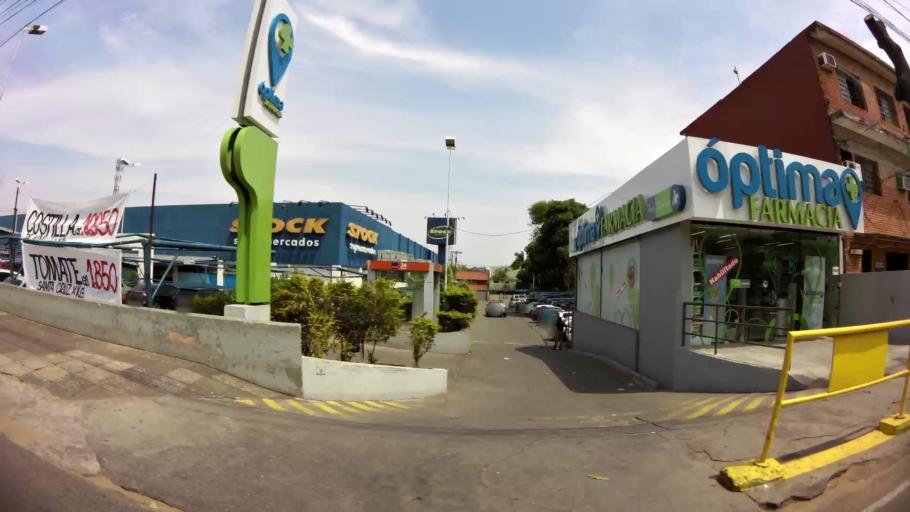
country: PY
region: Asuncion
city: Asuncion
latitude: -25.2722
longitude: -57.5846
